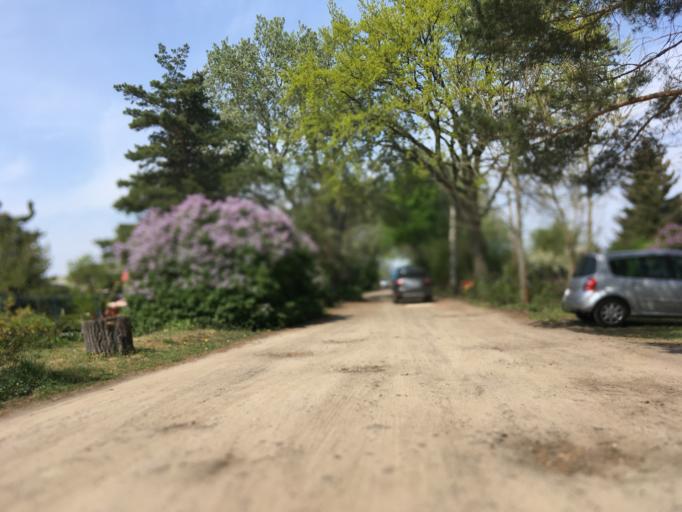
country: DE
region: Berlin
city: Karlshorst
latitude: 52.4788
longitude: 13.5436
